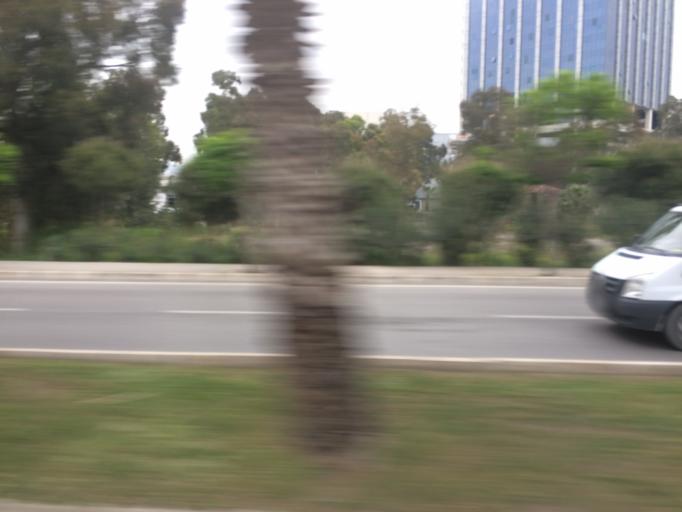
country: TR
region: Izmir
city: Izmir
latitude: 38.4531
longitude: 27.1688
